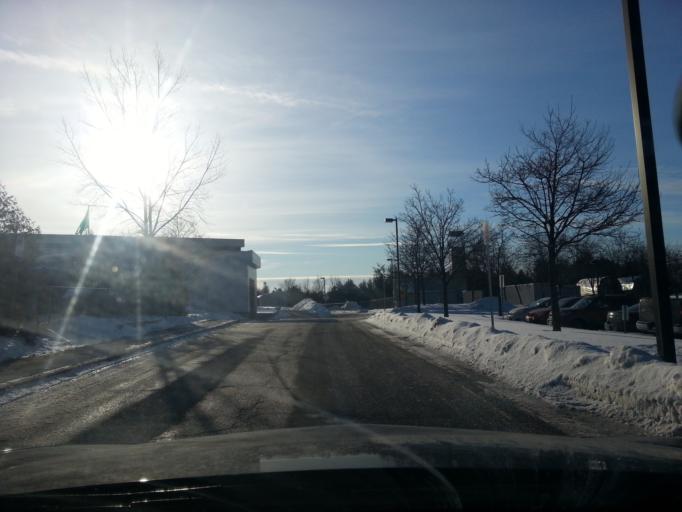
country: CA
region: Ontario
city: Ottawa
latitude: 45.4401
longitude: -75.6292
